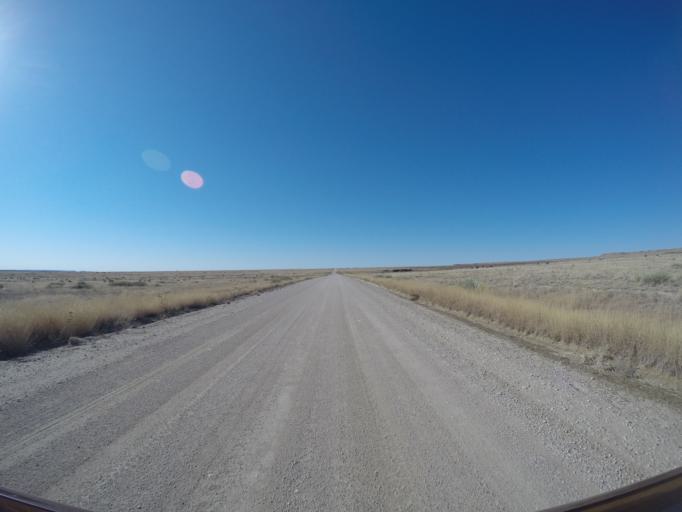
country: US
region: Colorado
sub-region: Otero County
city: La Junta
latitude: 37.7959
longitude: -103.5116
